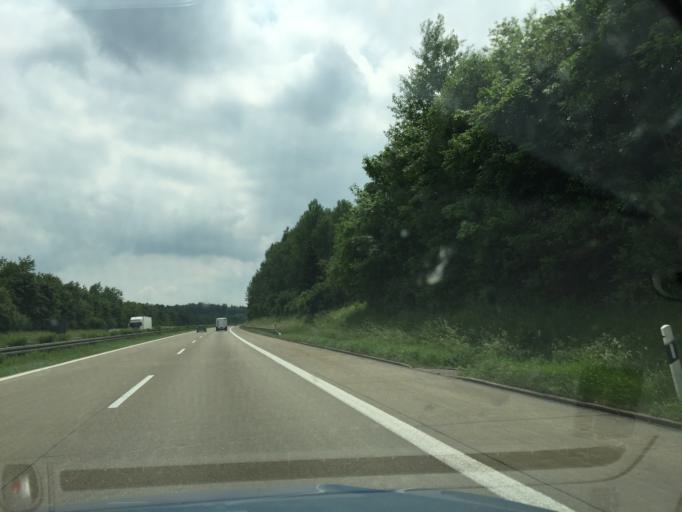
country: DE
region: Baden-Wuerttemberg
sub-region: Regierungsbezirk Stuttgart
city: Lauchheim
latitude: 48.7860
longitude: 10.2117
